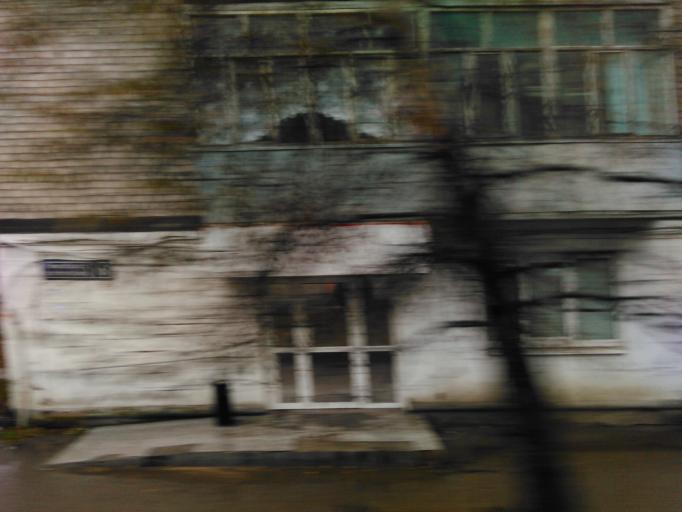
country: RU
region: Tatarstan
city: Osinovo
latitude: 55.8203
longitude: 48.8968
